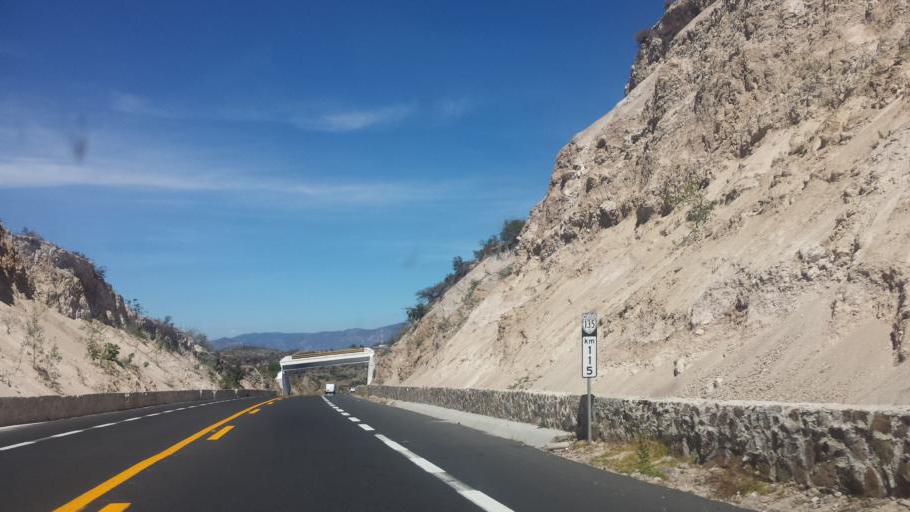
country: MX
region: Oaxaca
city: San Gabriel Casa Blanca
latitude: 17.9622
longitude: -97.3574
